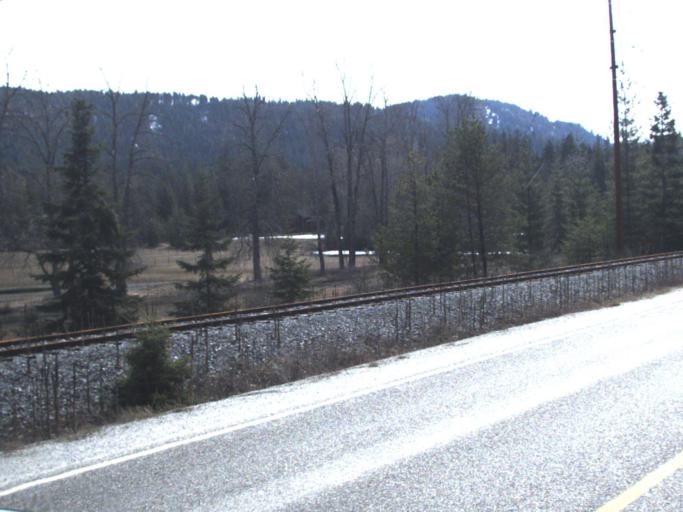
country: US
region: Washington
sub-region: Stevens County
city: Chewelah
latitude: 48.6200
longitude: -117.3660
